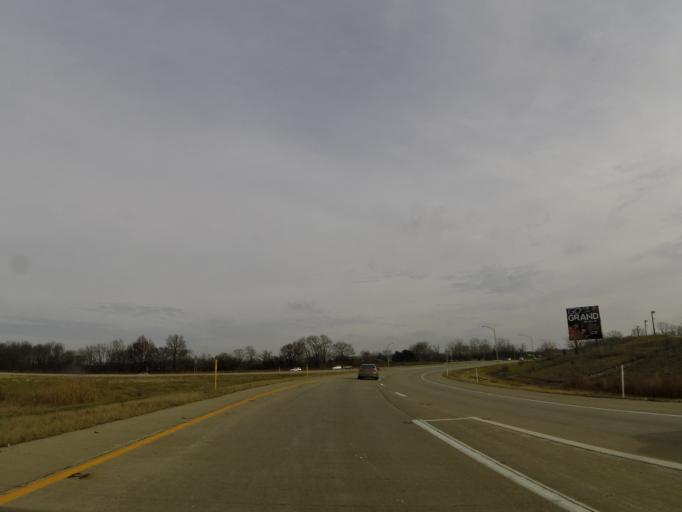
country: US
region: Indiana
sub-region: Marion County
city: Beech Grove
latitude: 39.7314
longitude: -86.0415
